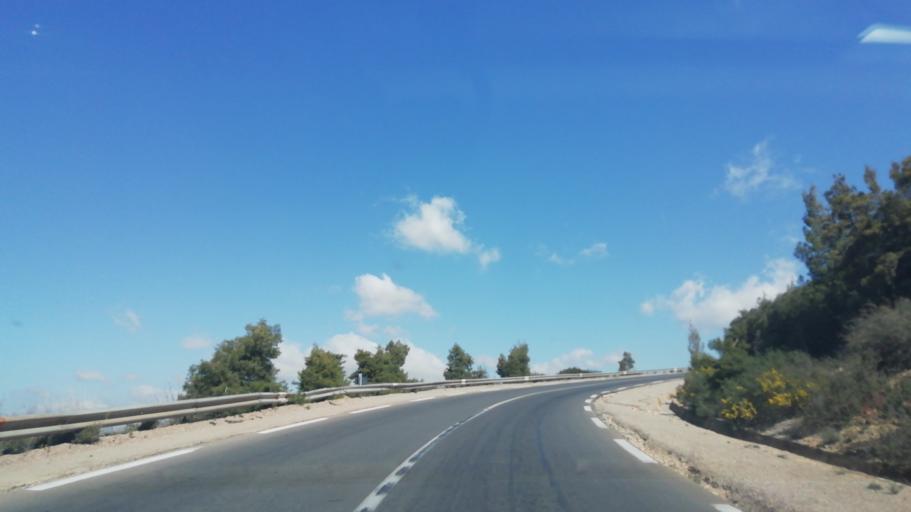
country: DZ
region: Mascara
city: Mascara
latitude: 35.4893
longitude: 0.1472
